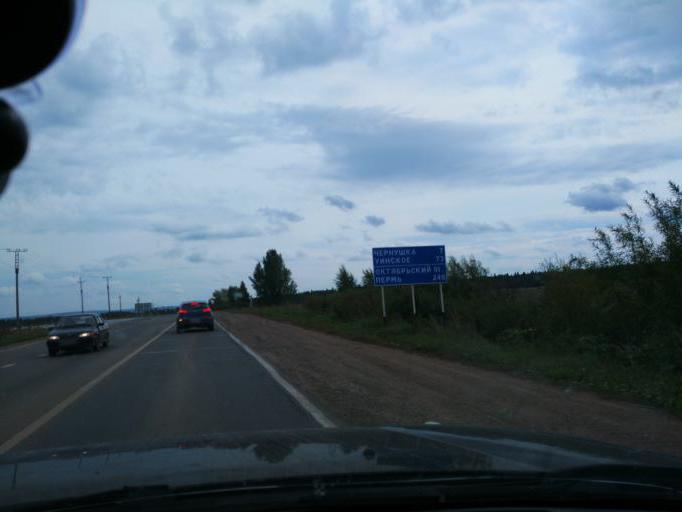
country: RU
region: Perm
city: Chernushka
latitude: 56.5048
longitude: 55.9879
